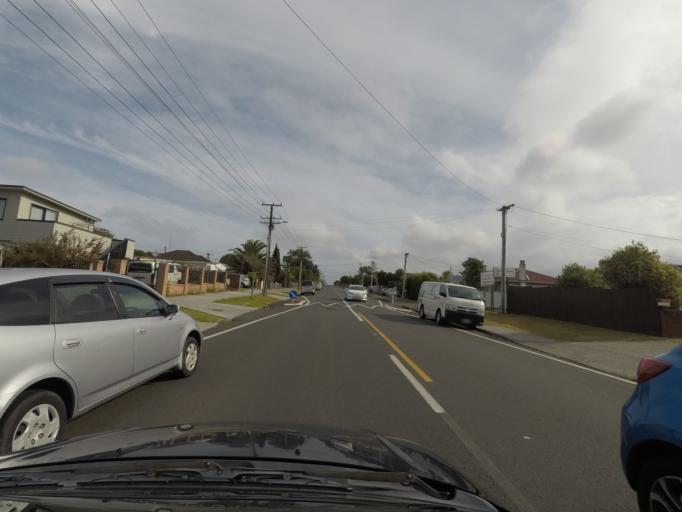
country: NZ
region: Auckland
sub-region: Auckland
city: Waitakere
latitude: -36.9015
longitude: 174.6660
